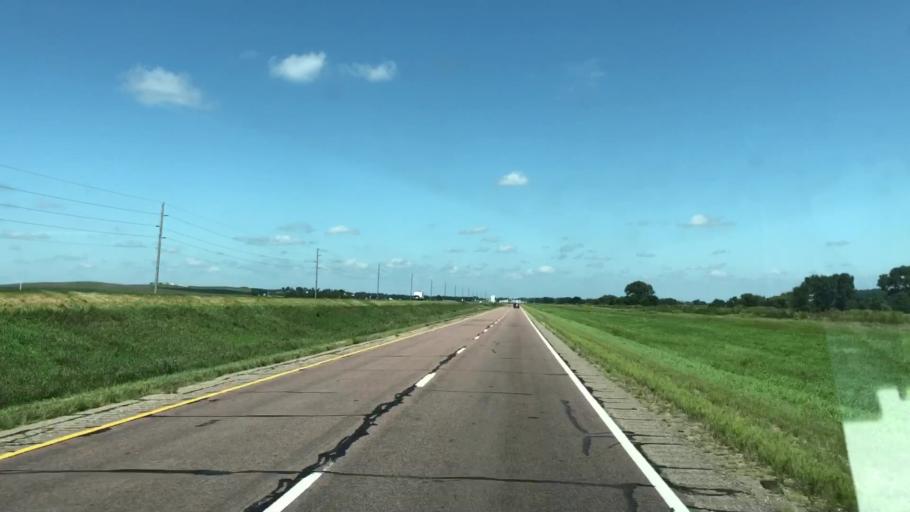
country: US
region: Iowa
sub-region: Plymouth County
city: Le Mars
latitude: 42.6854
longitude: -96.2658
